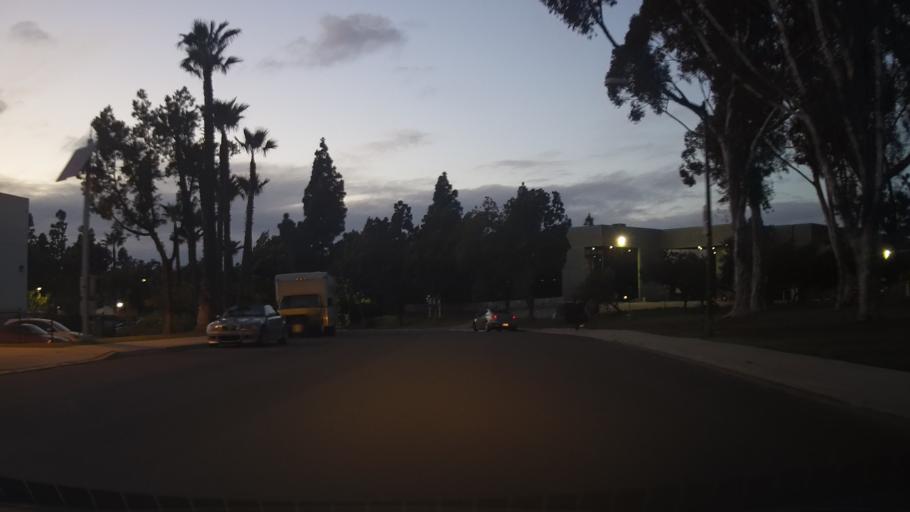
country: US
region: California
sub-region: San Diego County
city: National City
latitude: 32.7143
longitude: -117.1126
